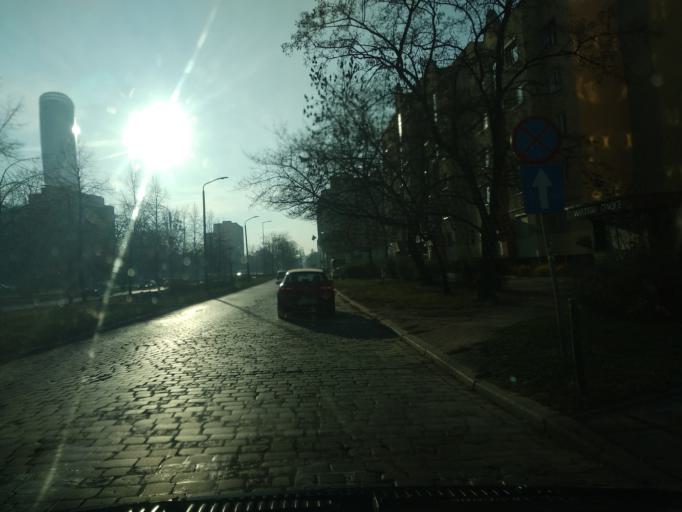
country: PL
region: Lower Silesian Voivodeship
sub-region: Powiat wroclawski
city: Wroclaw
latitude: 51.0999
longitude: 17.0137
